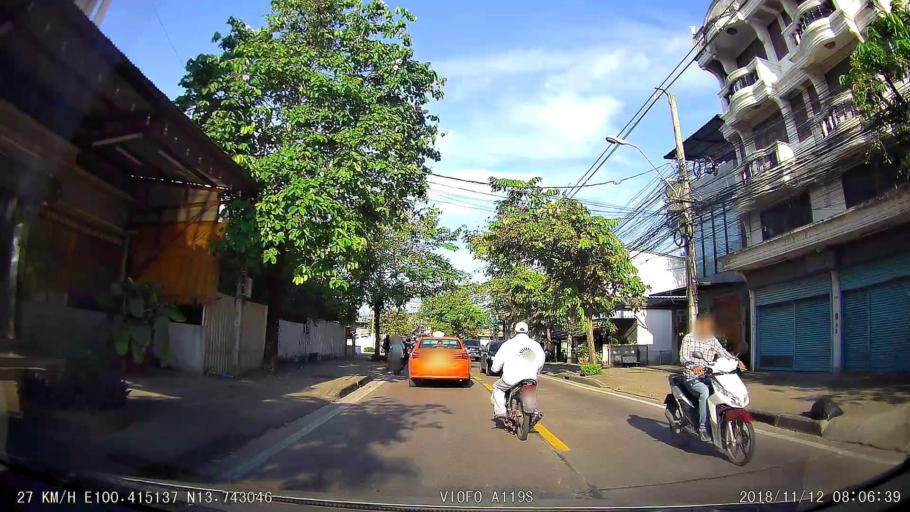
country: TH
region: Bangkok
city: Phasi Charoen
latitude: 13.7431
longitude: 100.4151
